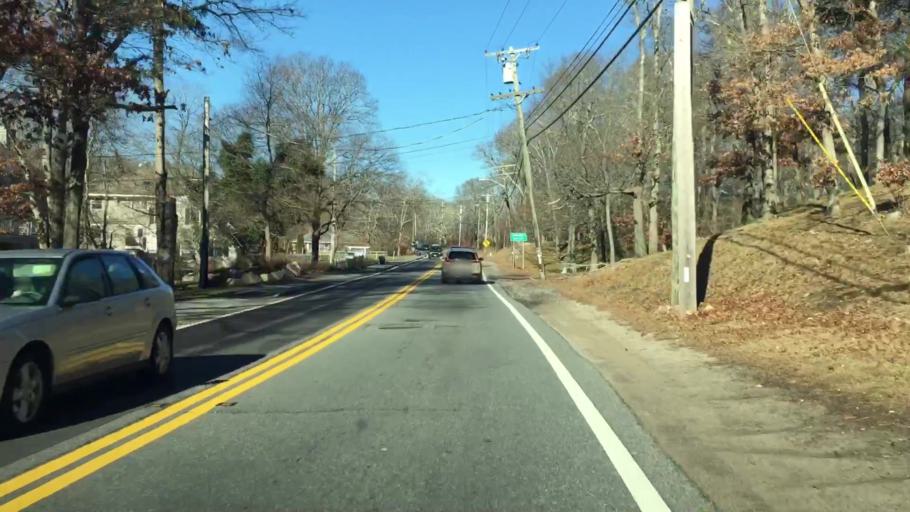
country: US
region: Massachusetts
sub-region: Barnstable County
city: Falmouth
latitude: 41.5683
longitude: -70.6173
